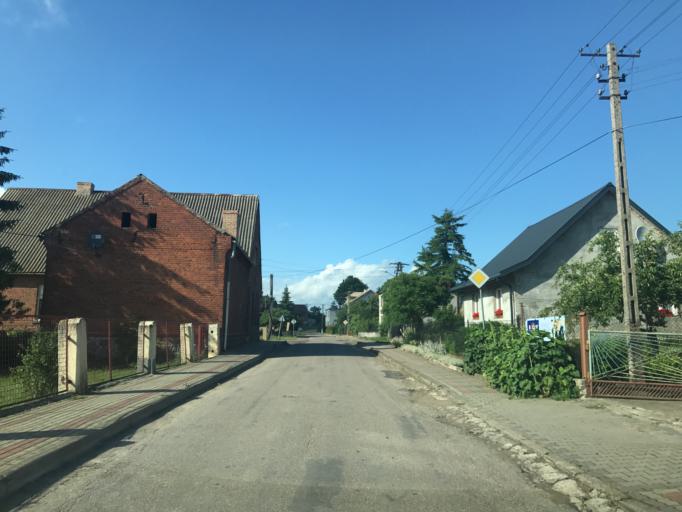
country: PL
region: Warmian-Masurian Voivodeship
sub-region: Powiat dzialdowski
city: Rybno
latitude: 53.3867
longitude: 19.8764
